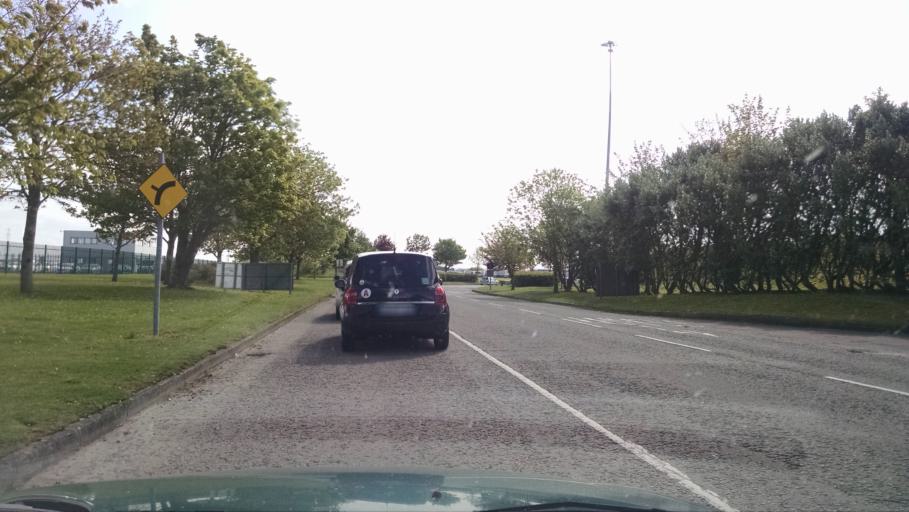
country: IE
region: Munster
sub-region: County Cork
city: Cobh
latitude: 51.8326
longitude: -8.3180
